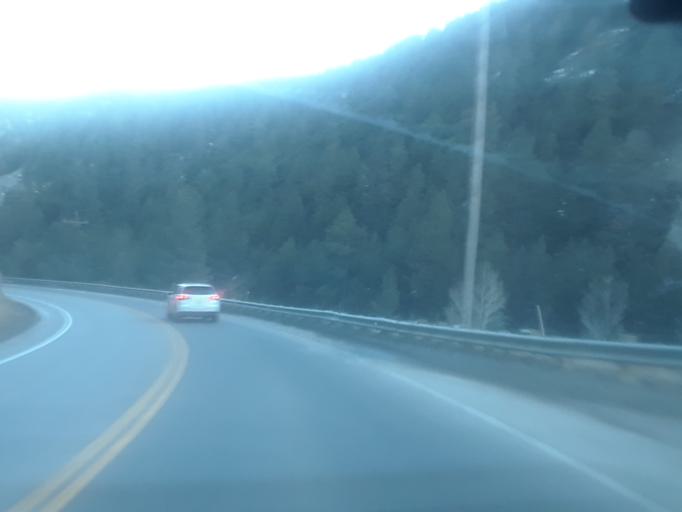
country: US
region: Colorado
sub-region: Clear Creek County
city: Idaho Springs
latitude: 39.7390
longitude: -105.4268
